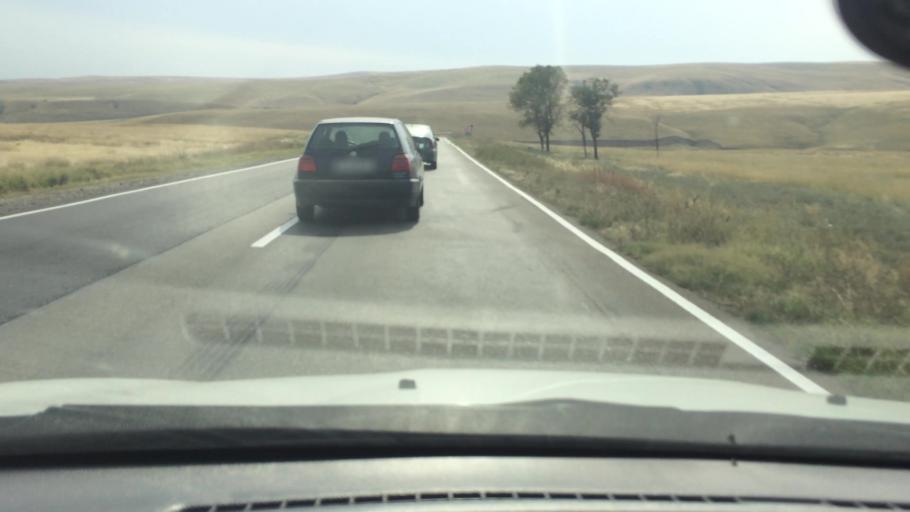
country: GE
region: Kvemo Kartli
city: Rust'avi
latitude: 41.5261
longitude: 44.9373
